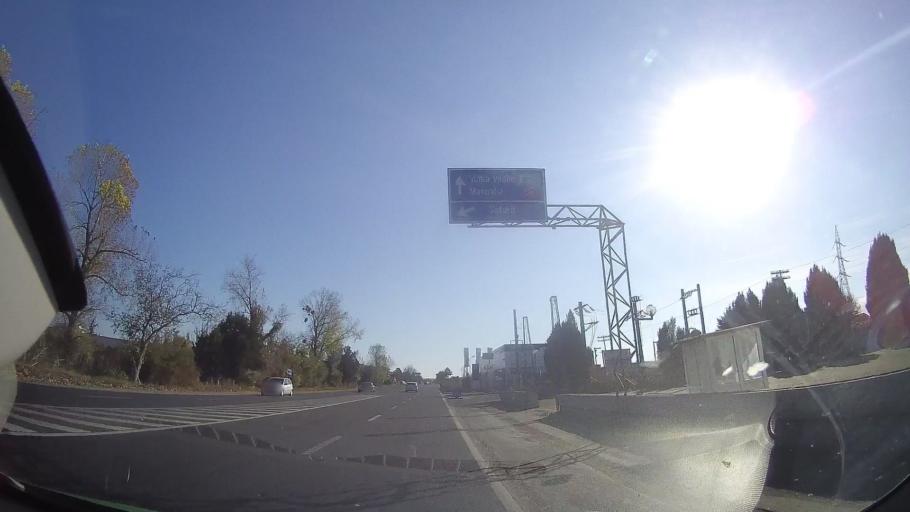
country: RO
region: Constanta
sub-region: Municipiul Mangalia
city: Mangalia
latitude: 43.8313
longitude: 28.5790
